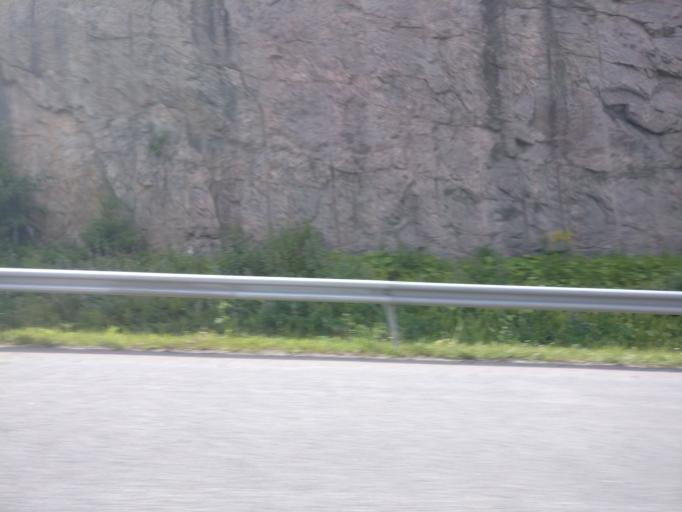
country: FI
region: Paijanne Tavastia
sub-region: Lahti
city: Lahti
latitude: 60.9640
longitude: 25.7067
